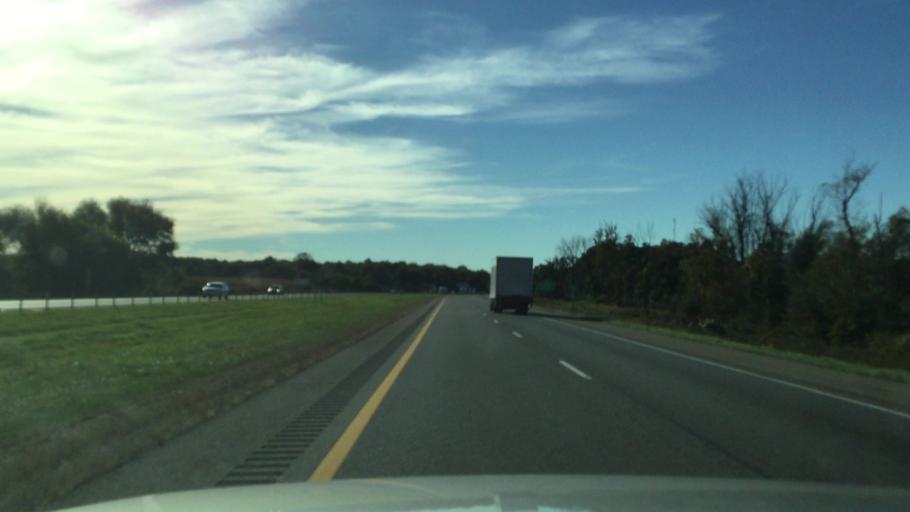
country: US
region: Michigan
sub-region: Calhoun County
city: Brownlee Park
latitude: 42.2979
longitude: -85.0584
